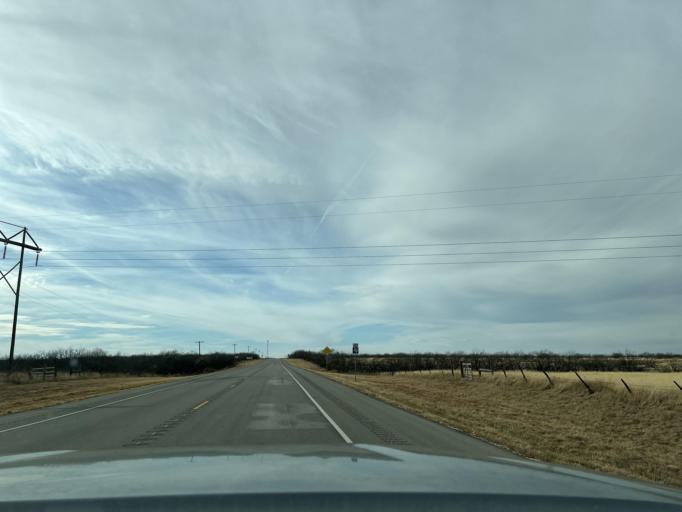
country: US
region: Texas
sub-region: Jones County
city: Anson
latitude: 32.7506
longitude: -99.7076
